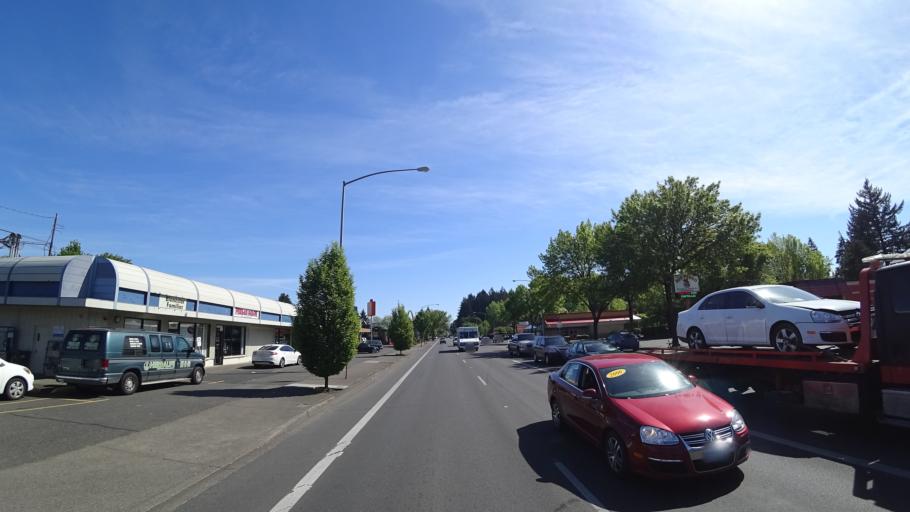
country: US
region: Oregon
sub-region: Washington County
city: Hillsboro
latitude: 45.5173
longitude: -122.9739
